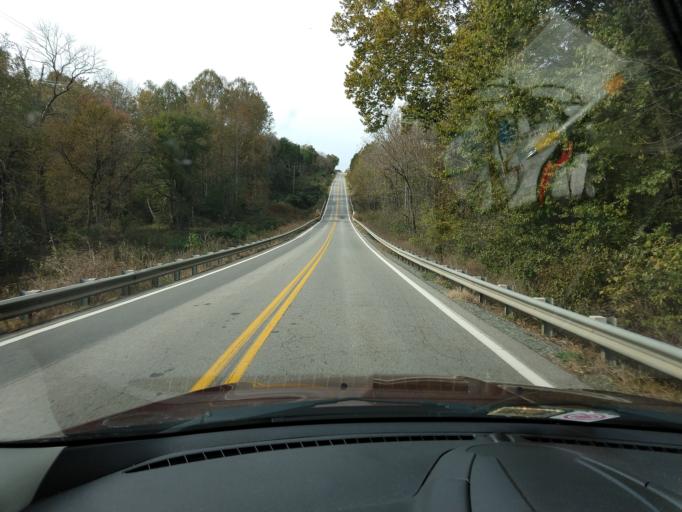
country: US
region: Virginia
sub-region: Pittsylvania County
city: Gretna
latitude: 36.9445
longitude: -79.4894
